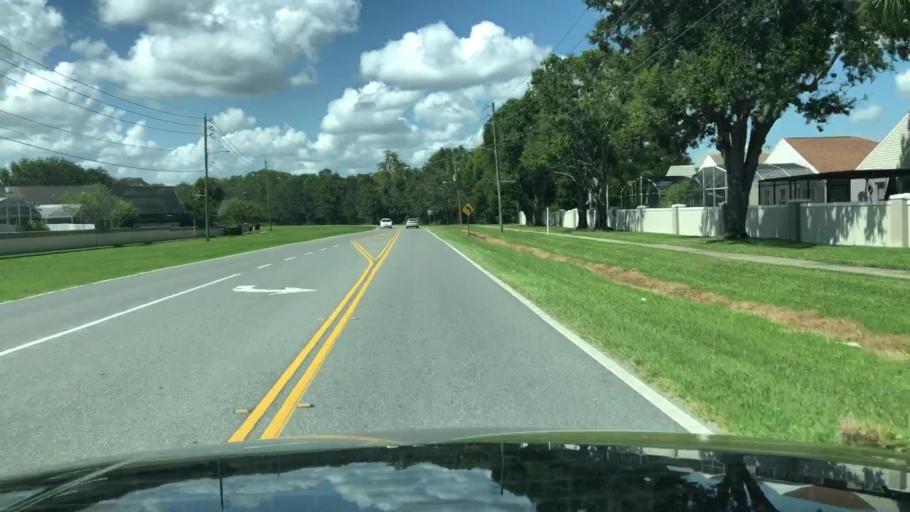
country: US
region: Florida
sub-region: Osceola County
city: Celebration
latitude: 28.3186
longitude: -81.4804
